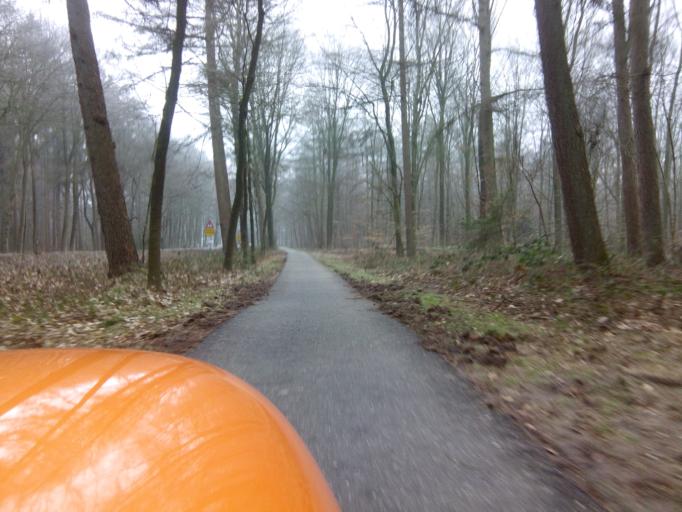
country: NL
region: Gelderland
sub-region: Gemeente Putten
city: Putten
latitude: 52.2387
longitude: 5.6531
